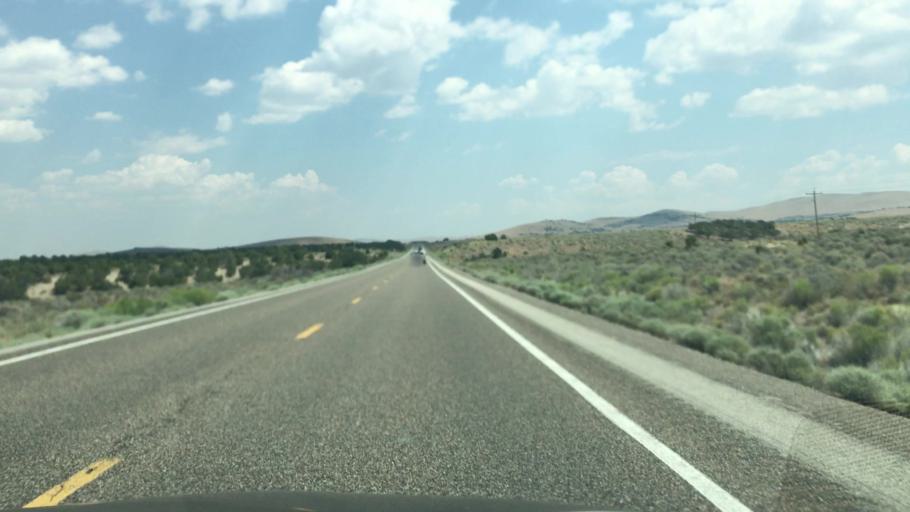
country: US
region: Nevada
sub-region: Elko County
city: Wells
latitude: 41.1970
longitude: -114.8621
